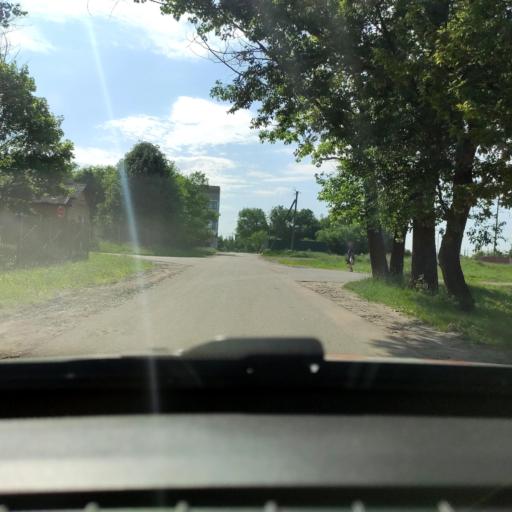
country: RU
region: Voronezj
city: Semiluki
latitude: 51.7019
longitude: 39.0266
